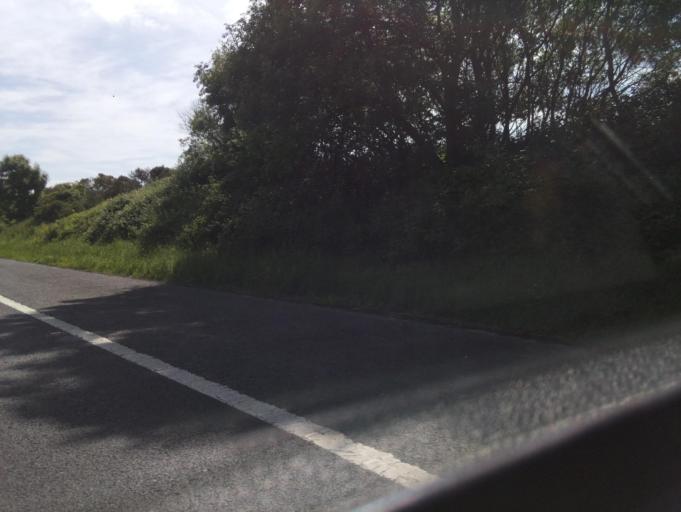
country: GB
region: England
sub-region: North Lincolnshire
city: Bottesford
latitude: 53.5464
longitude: -0.6289
